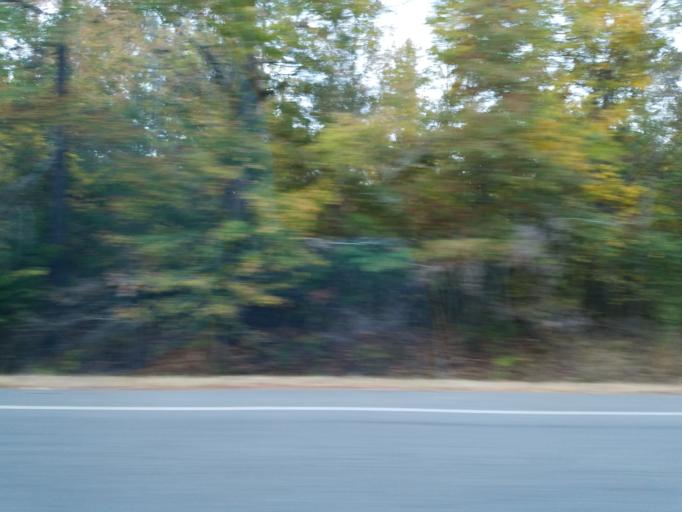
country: US
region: Georgia
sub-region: Gordon County
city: Calhoun
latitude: 34.6083
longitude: -85.0445
